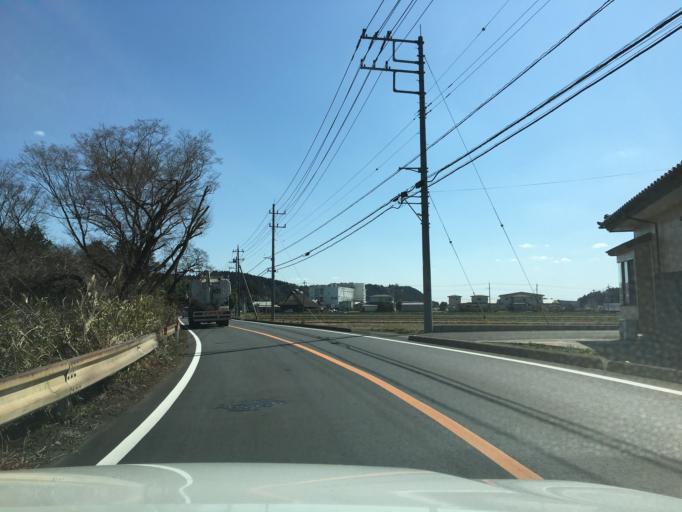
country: JP
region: Tochigi
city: Otawara
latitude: 36.8843
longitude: 140.1179
